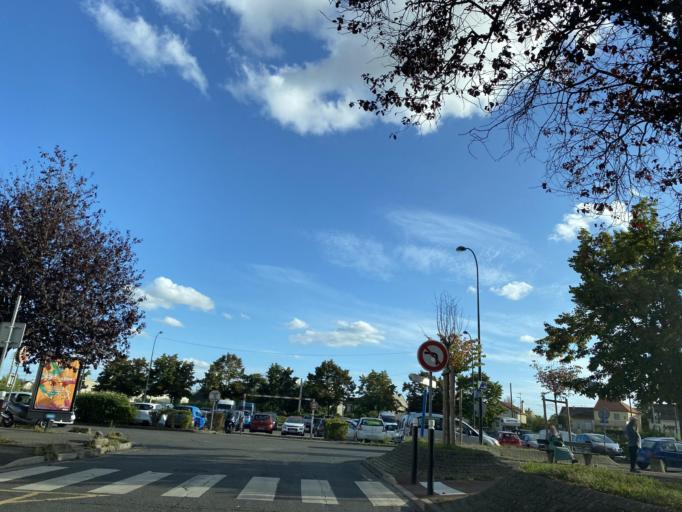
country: FR
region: Ile-de-France
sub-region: Departement des Yvelines
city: Sartrouville
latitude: 48.9407
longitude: 2.1938
